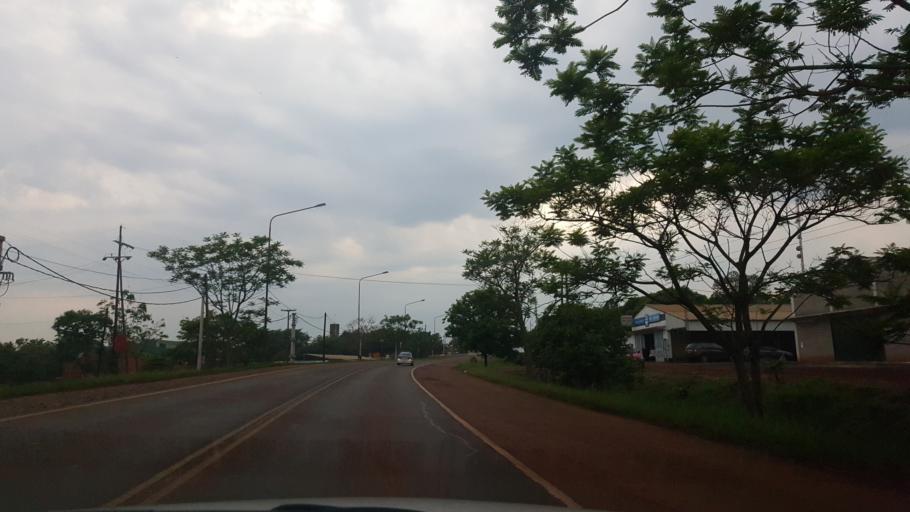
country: AR
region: Misiones
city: Jardin America
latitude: -27.0495
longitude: -55.2470
